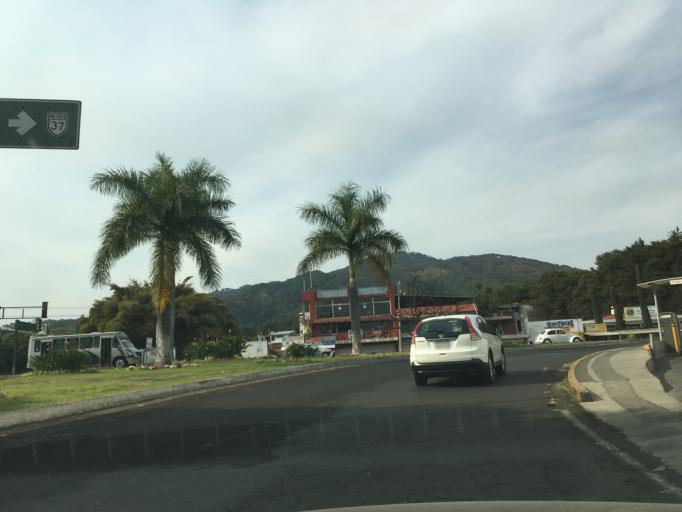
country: MX
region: Michoacan
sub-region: Uruapan
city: Uruapan
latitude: 19.4252
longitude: -102.0481
